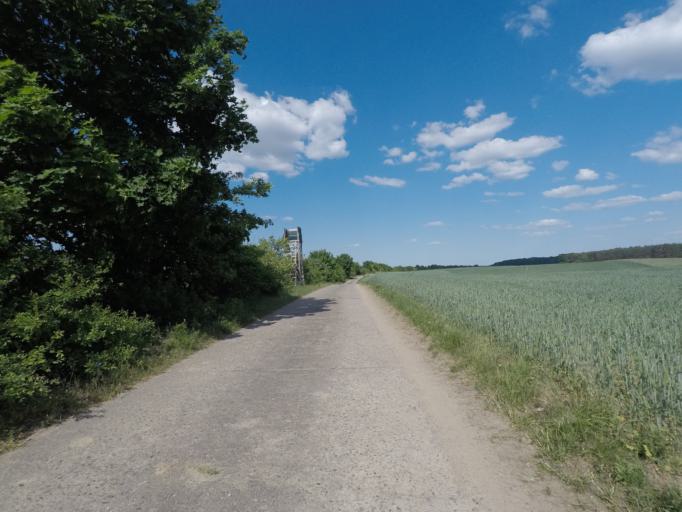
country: DE
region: Brandenburg
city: Melchow
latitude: 52.8666
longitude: 13.6938
